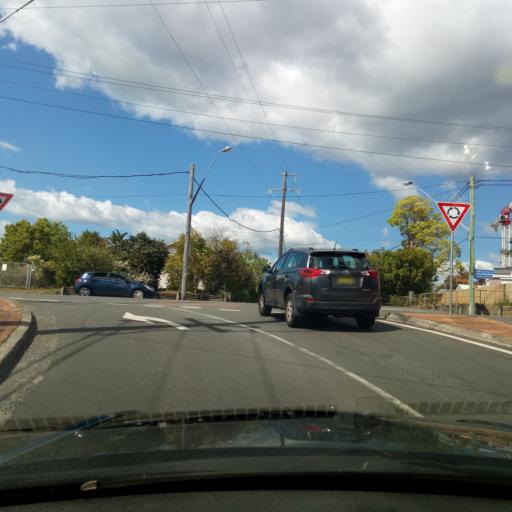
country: AU
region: New South Wales
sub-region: Gosford Shire
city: Gosford
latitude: -33.4187
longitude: 151.3423
